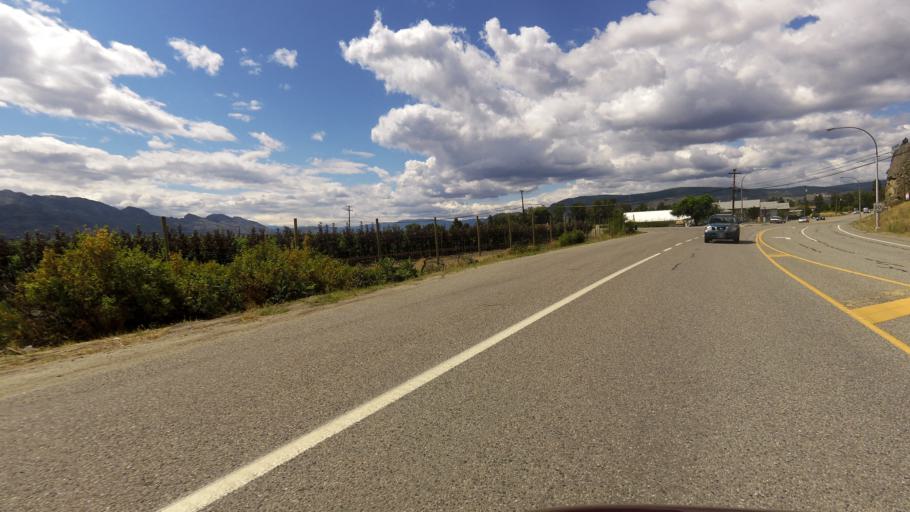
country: CA
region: British Columbia
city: West Kelowna
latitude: 49.8310
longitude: -119.5875
